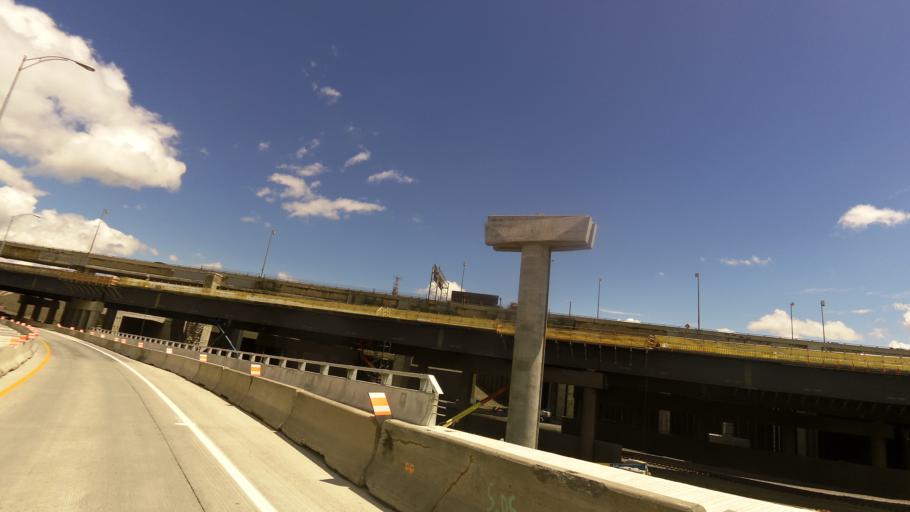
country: CA
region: Quebec
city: Saint-Raymond
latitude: 45.4697
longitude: -73.5996
